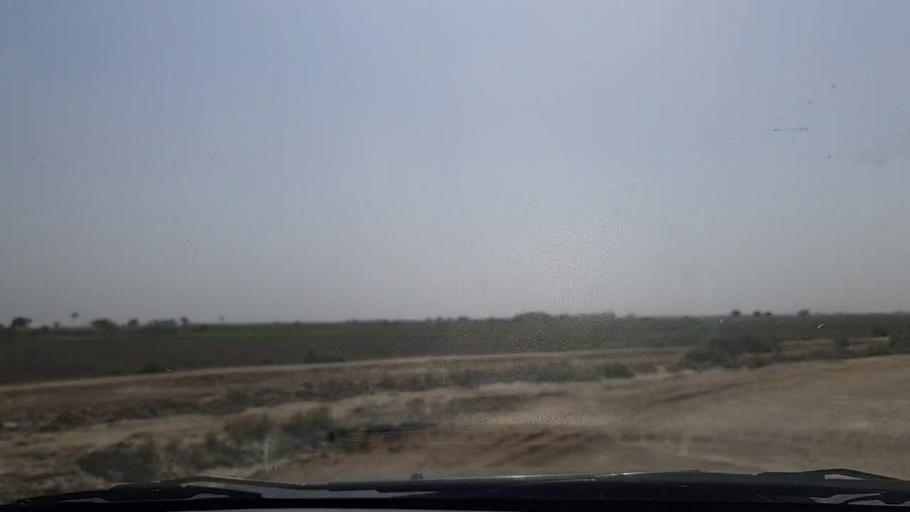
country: PK
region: Sindh
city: Keti Bandar
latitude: 24.2686
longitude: 67.6731
